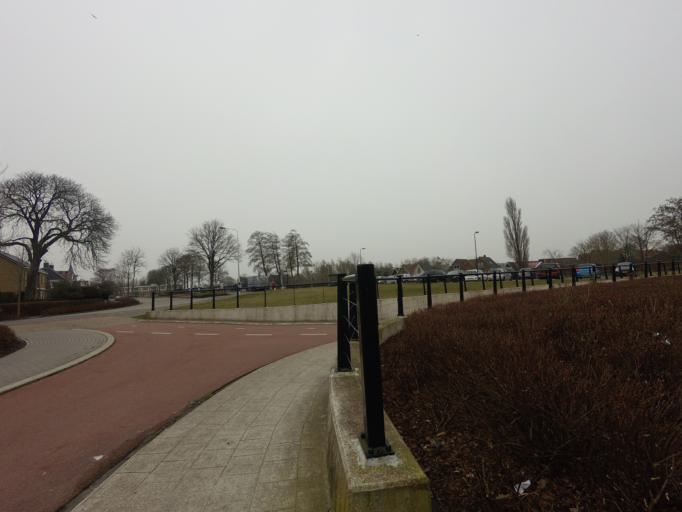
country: NL
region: Friesland
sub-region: Gemeente Franekeradeel
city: Franeker
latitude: 53.1828
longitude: 5.5479
